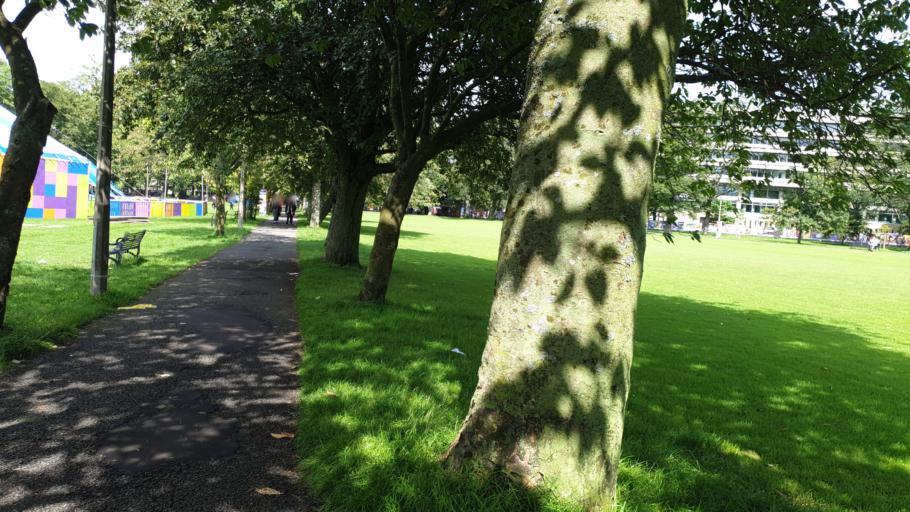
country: GB
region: Scotland
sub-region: Edinburgh
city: Edinburgh
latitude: 55.9410
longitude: -3.1888
